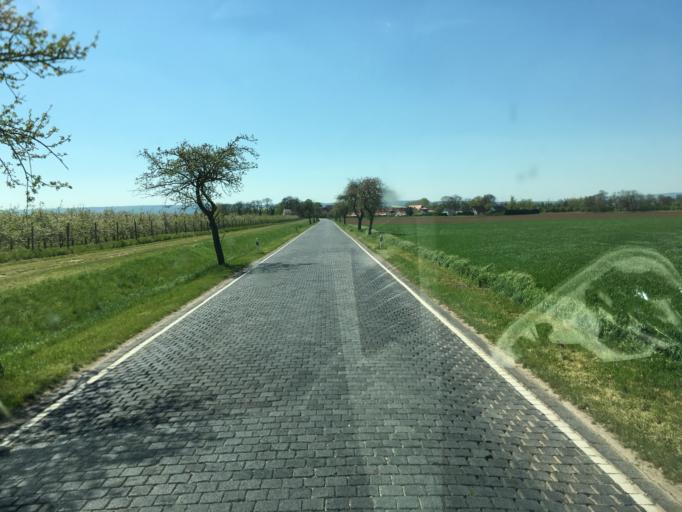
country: DE
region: Thuringia
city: Monchpfiffel-Nikolausrieth
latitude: 51.3839
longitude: 11.3772
